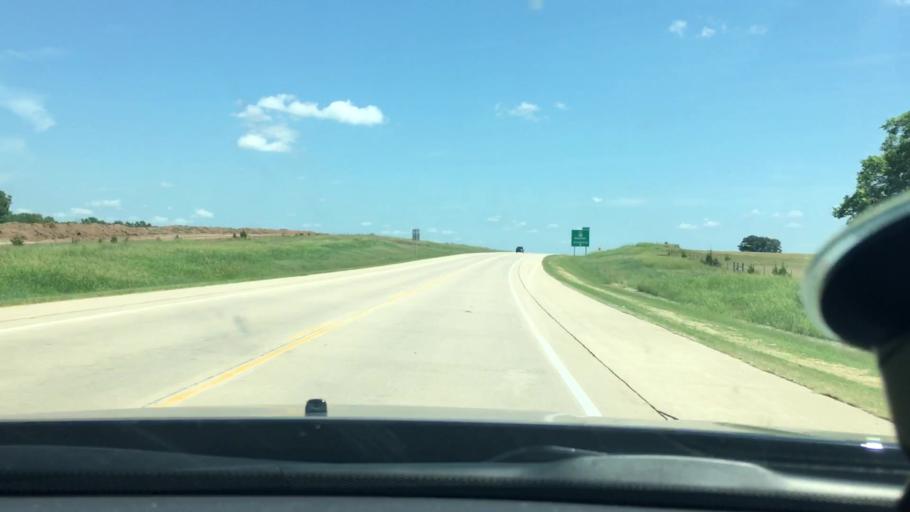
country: US
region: Oklahoma
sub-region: Murray County
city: Sulphur
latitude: 34.5426
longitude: -96.9785
